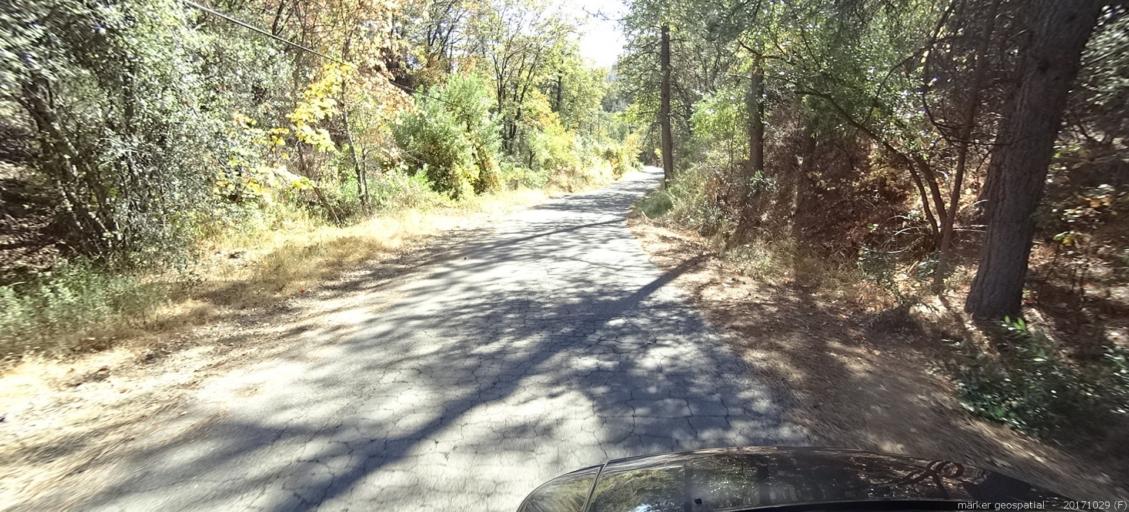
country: US
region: California
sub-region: Shasta County
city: Shasta
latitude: 40.4932
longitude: -122.6892
